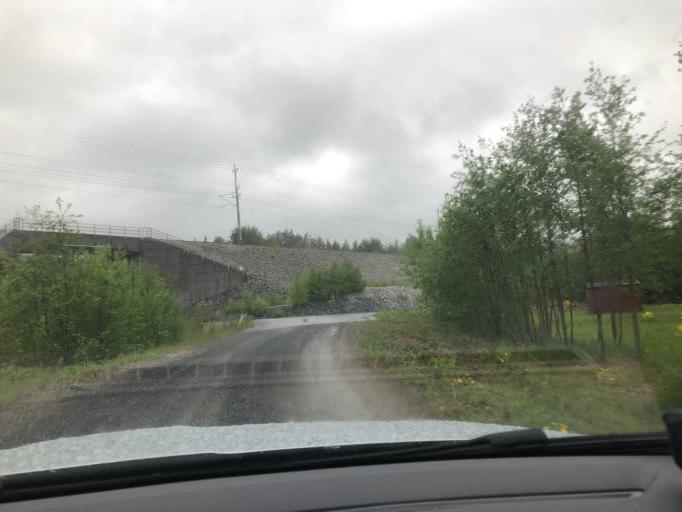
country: SE
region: Vaesternorrland
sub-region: Haernoesands Kommun
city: Haernoesand
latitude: 62.7938
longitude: 17.9239
